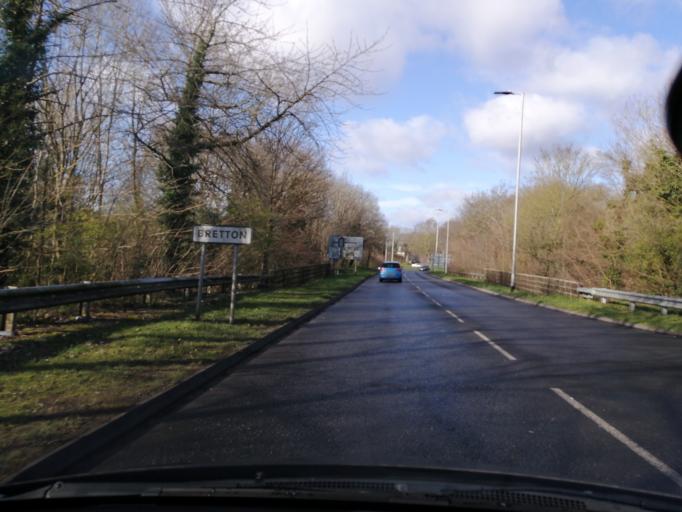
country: GB
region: England
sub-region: Peterborough
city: Marholm
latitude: 52.5878
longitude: -0.2830
